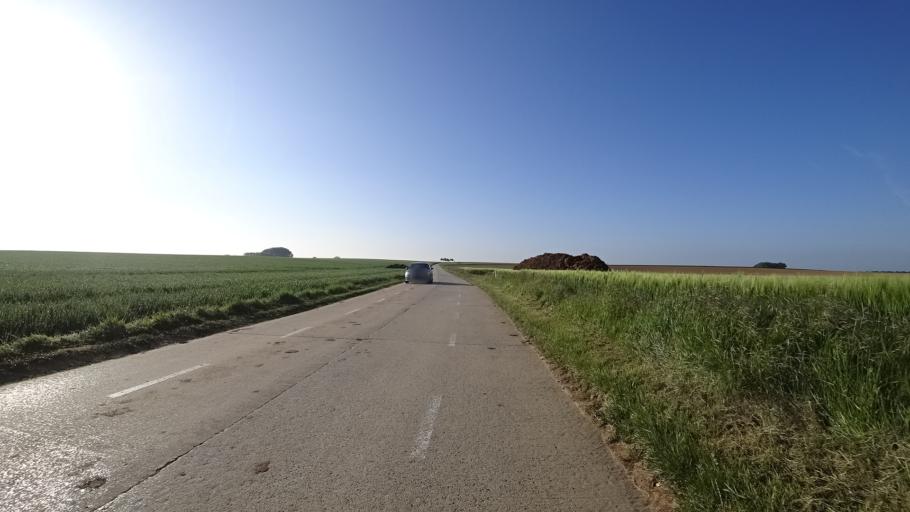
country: BE
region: Wallonia
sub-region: Province du Brabant Wallon
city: Walhain-Saint-Paul
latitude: 50.6319
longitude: 4.6830
